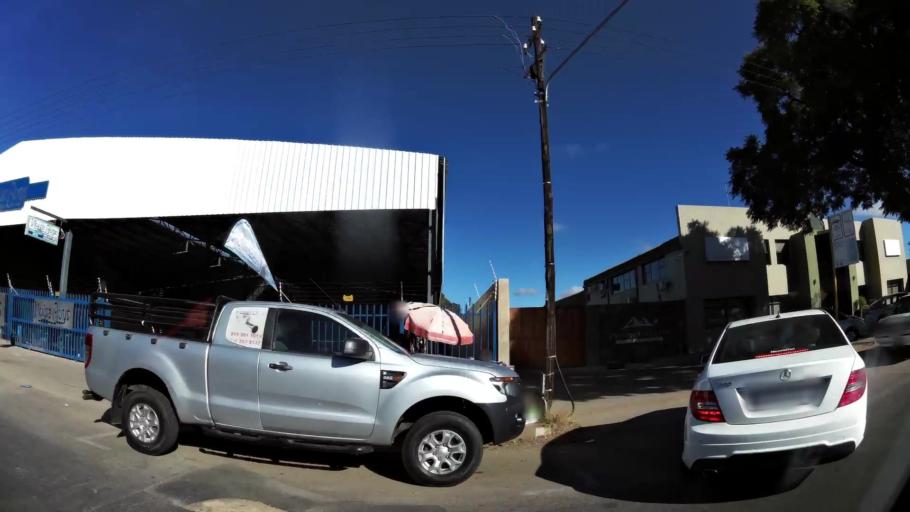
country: ZA
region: Limpopo
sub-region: Capricorn District Municipality
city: Polokwane
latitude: -23.9083
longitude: 29.4494
